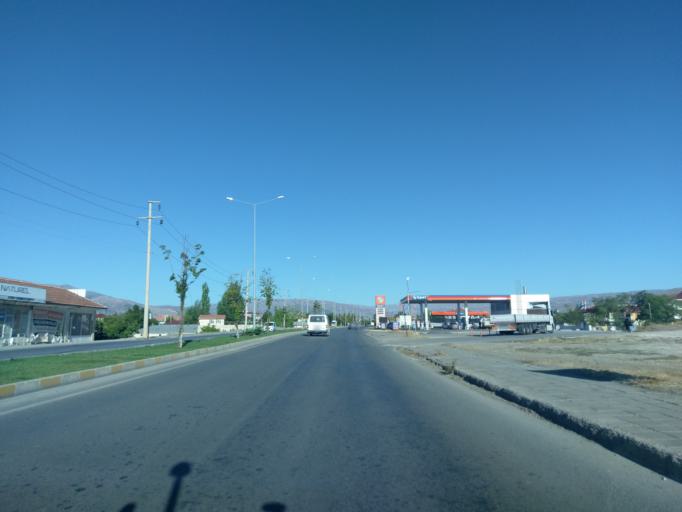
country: TR
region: Erzincan
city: Erzincan
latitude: 39.7506
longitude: 39.4587
